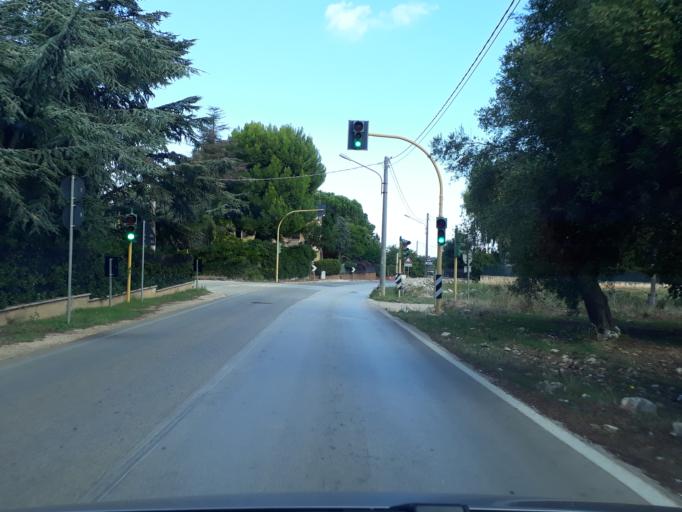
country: IT
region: Apulia
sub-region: Provincia di Bari
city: Mola di Bari
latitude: 41.0365
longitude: 17.0484
